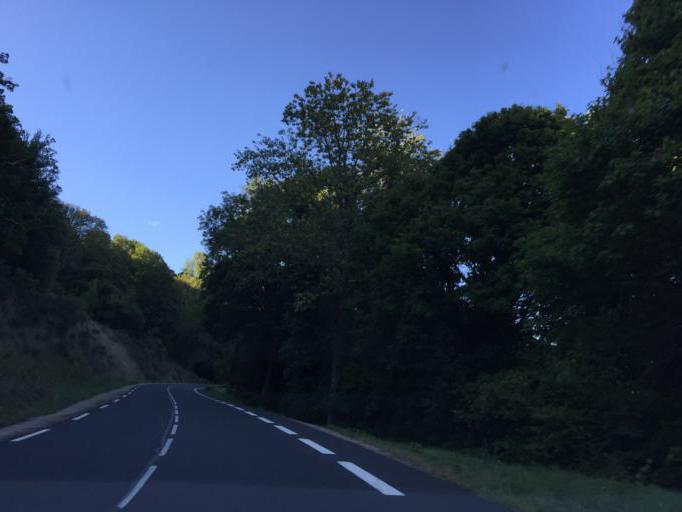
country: FR
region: Auvergne
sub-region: Departement de la Haute-Loire
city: Bains
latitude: 44.9736
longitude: 3.6714
